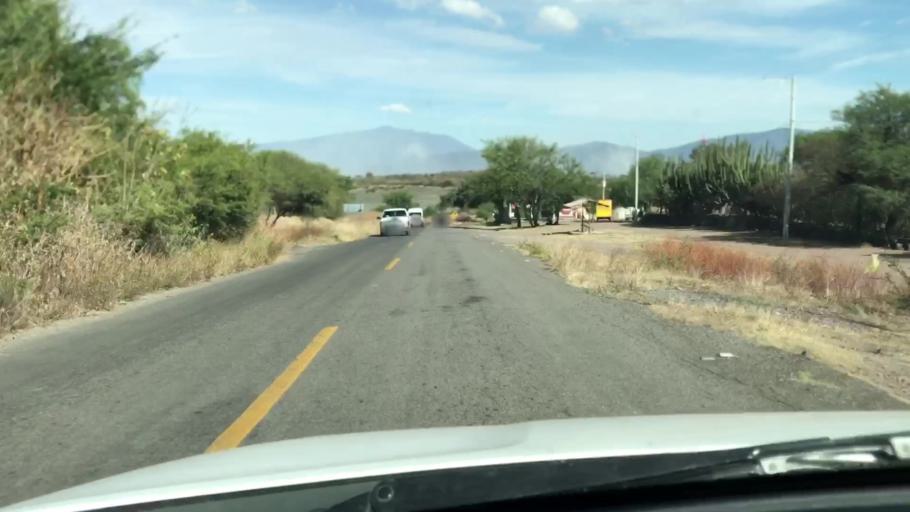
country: MX
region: Jalisco
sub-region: Zacoalco de Torres
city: Barranca de Otates (Barranca de Otatan)
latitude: 20.2583
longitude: -103.6648
